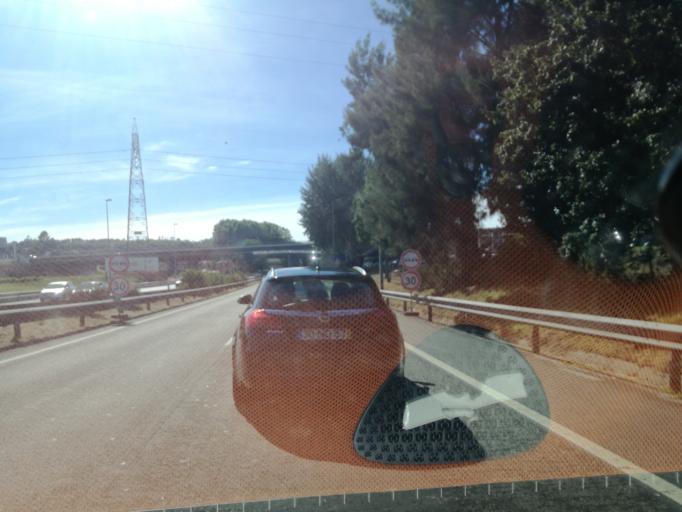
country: PT
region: Braga
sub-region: Guimaraes
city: Candoso
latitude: 41.4397
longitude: -8.3271
